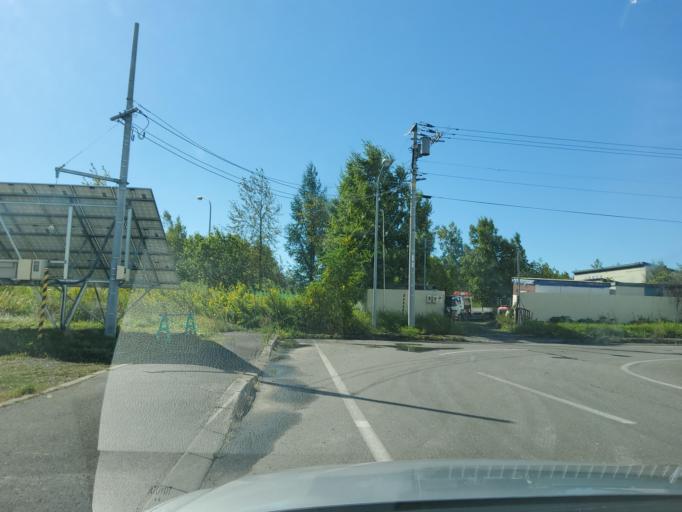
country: JP
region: Hokkaido
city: Otofuke
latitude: 42.9824
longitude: 143.1794
